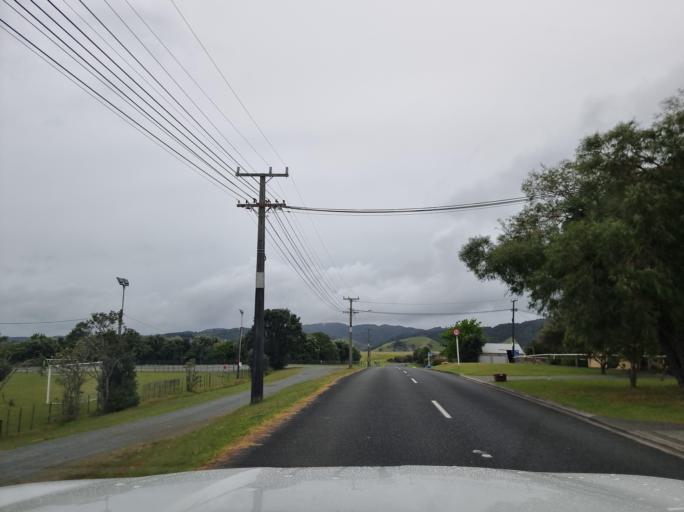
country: NZ
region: Northland
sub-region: Whangarei
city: Whangarei
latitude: -35.7707
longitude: 174.3670
